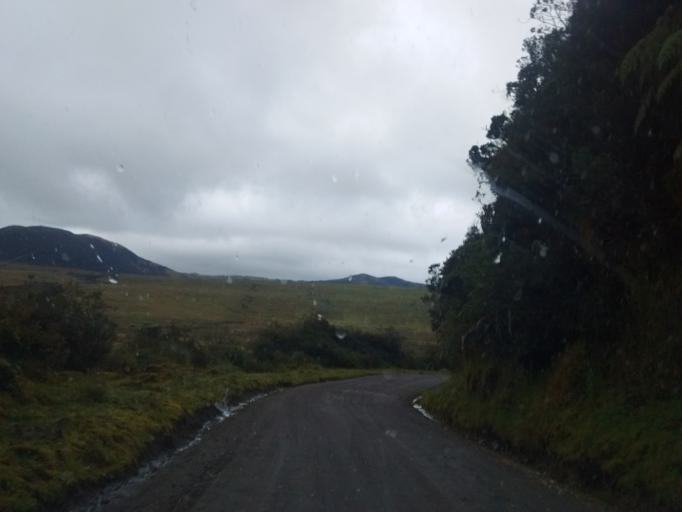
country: CO
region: Cauca
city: Totoro
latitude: 2.3548
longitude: -76.3281
